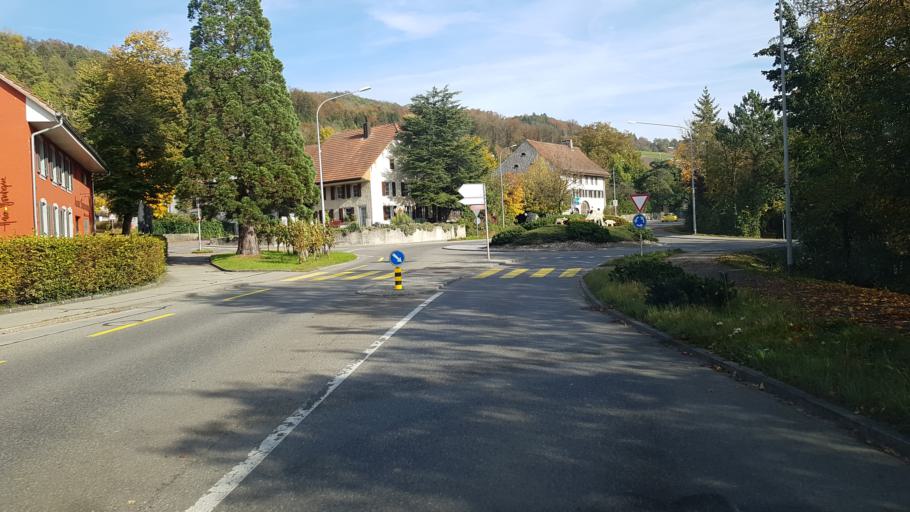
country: CH
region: Aargau
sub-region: Bezirk Baden
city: Birmenstorf
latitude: 47.4598
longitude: 8.2509
